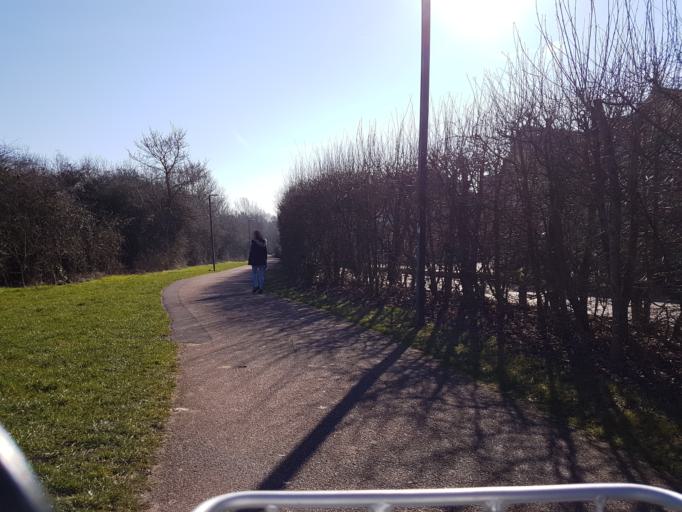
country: GB
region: England
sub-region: Milton Keynes
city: Loughton
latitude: 52.0122
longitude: -0.7636
